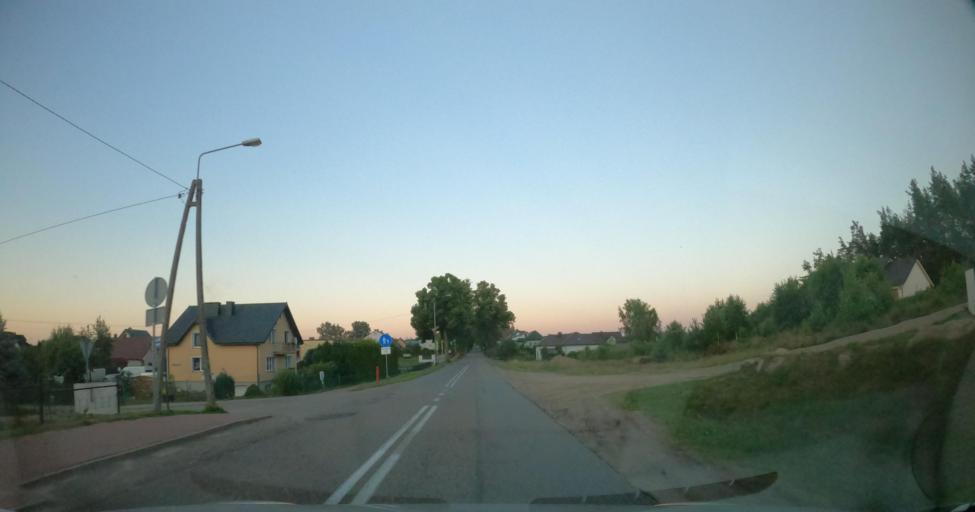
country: PL
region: Pomeranian Voivodeship
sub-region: Powiat wejherowski
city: Linia
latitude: 54.4572
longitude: 18.0146
